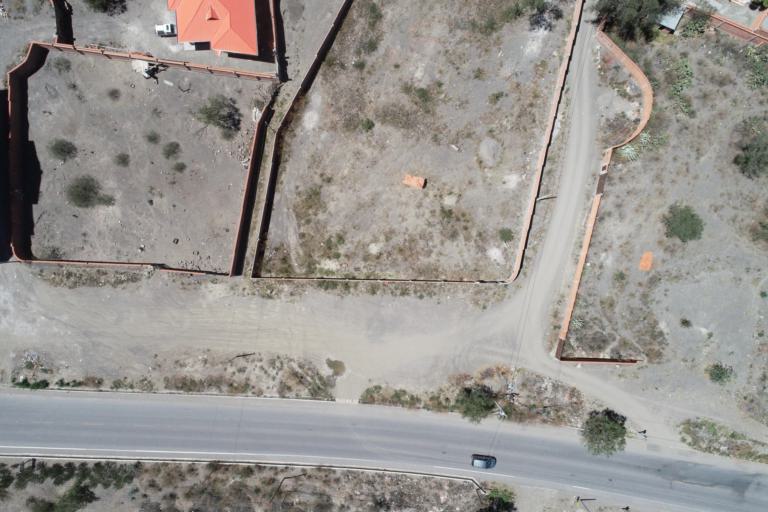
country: BO
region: La Paz
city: La Paz
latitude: -16.6266
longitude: -68.0524
